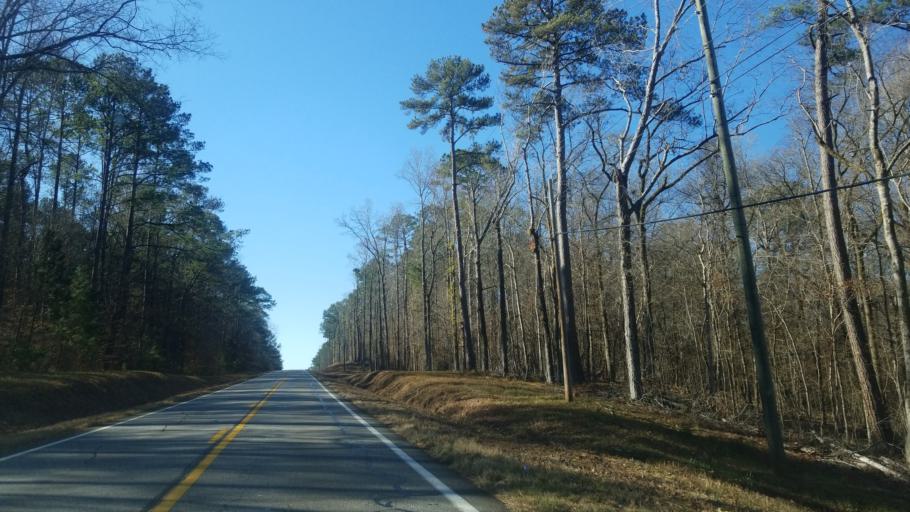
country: US
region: Alabama
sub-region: Lee County
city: Smiths Station
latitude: 32.6896
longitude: -85.0329
